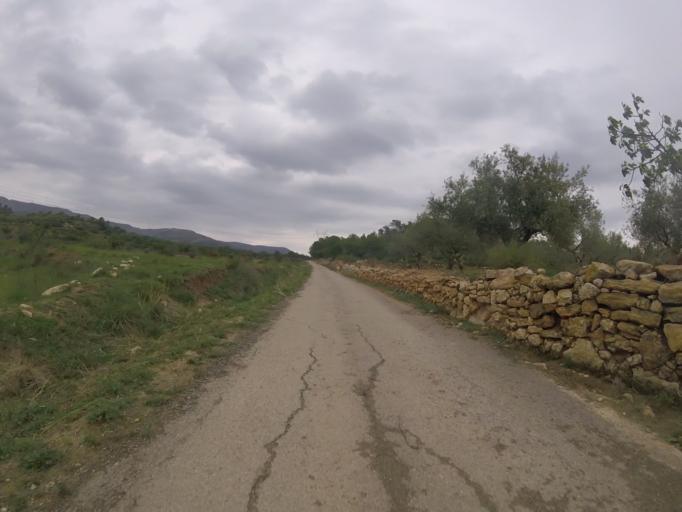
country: ES
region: Valencia
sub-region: Provincia de Castello
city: Sarratella
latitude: 40.2731
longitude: 0.0714
